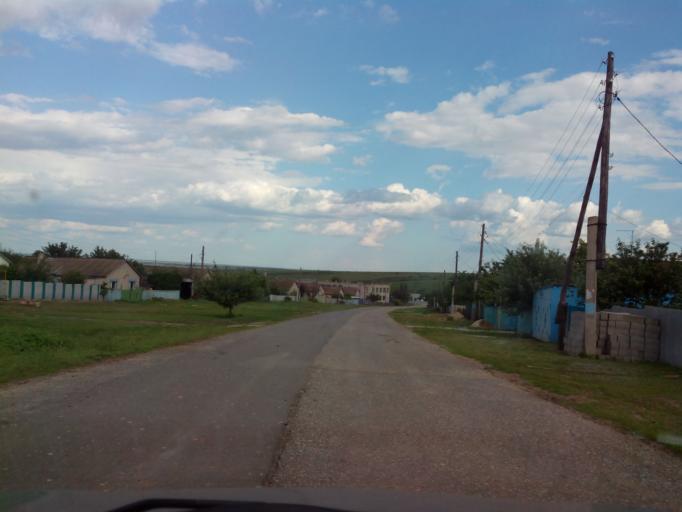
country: RU
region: Volgograd
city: Slashchevskaya
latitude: 49.7801
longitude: 42.4378
